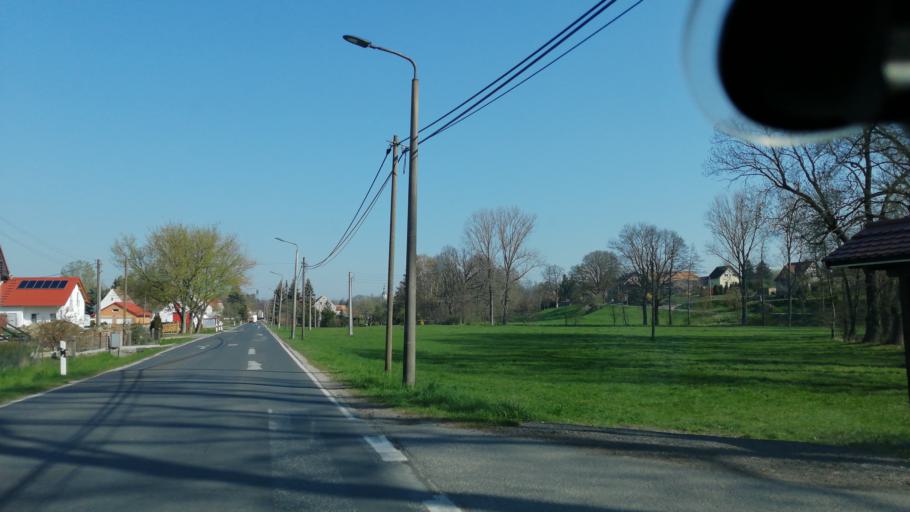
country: DE
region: Saxony
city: Goerlitz
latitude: 51.1705
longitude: 14.9355
